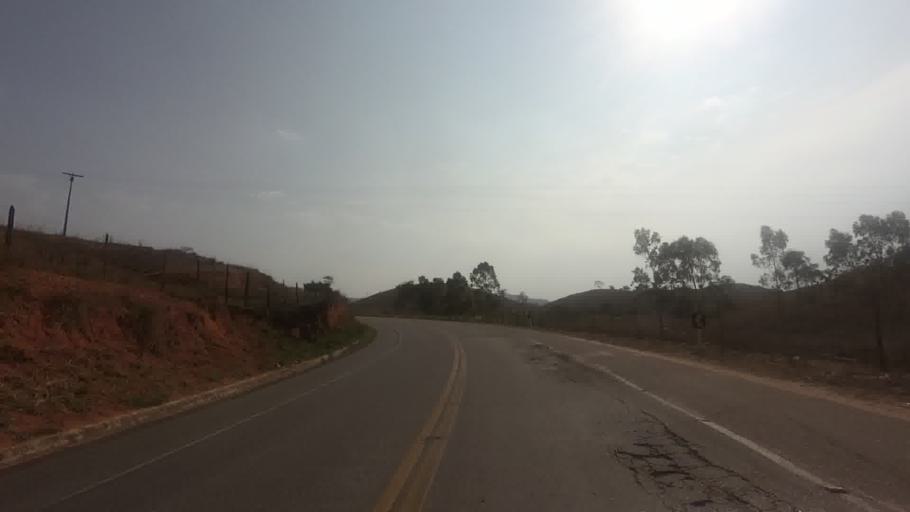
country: BR
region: Rio de Janeiro
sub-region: Bom Jesus Do Itabapoana
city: Bom Jesus do Itabapoana
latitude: -21.1311
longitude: -41.6477
